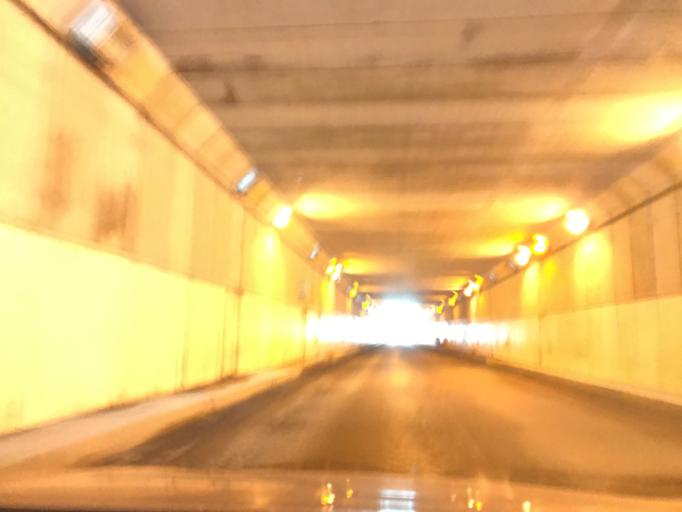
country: JP
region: Nagano
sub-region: Kitaazumi Gun
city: Hakuba
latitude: 36.7133
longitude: 137.8590
